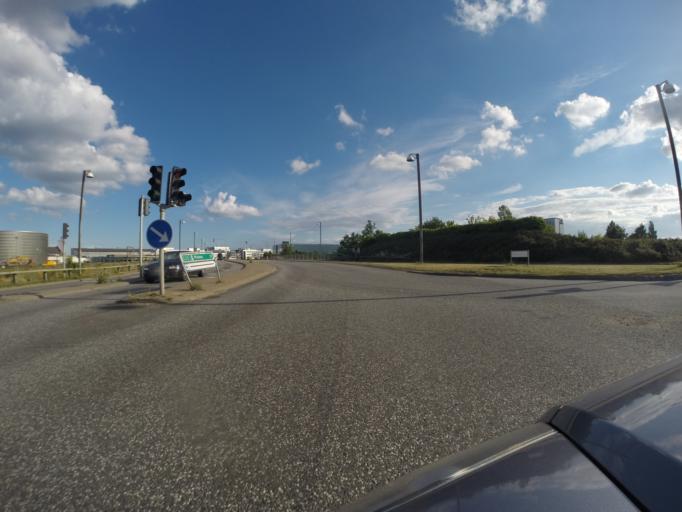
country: DK
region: Capital Region
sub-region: Dragor Kommune
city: Dragor
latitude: 55.6330
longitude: 12.6556
